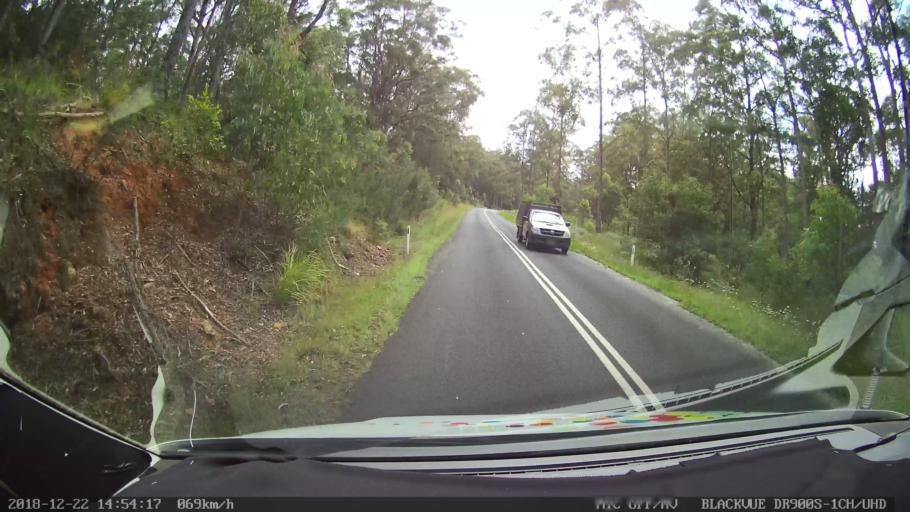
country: AU
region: New South Wales
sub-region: Bellingen
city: Dorrigo
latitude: -30.2253
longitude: 152.5341
